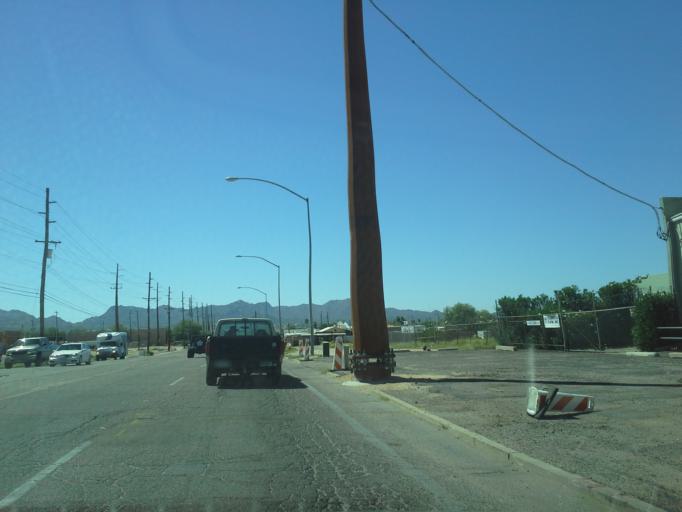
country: US
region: Arizona
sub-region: Pima County
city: Tucson
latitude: 32.2504
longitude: -110.9683
